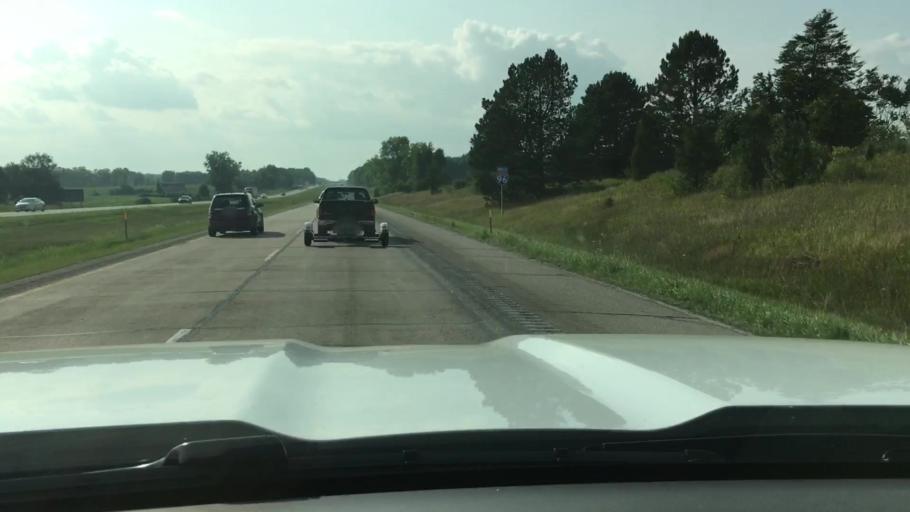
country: US
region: Michigan
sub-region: Eaton County
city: Grand Ledge
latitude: 42.8146
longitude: -84.7955
